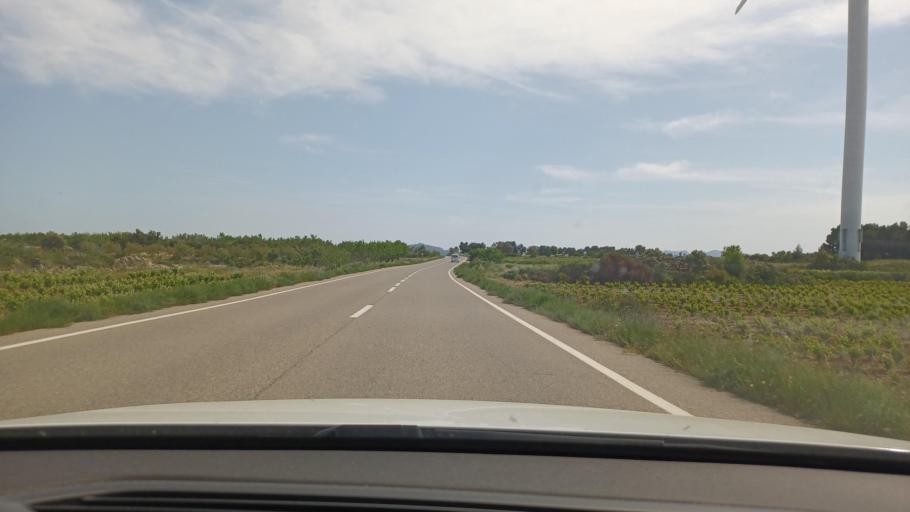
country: ES
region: Catalonia
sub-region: Provincia de Tarragona
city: Vilalba dels Arcs
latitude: 41.0968
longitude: 0.4179
